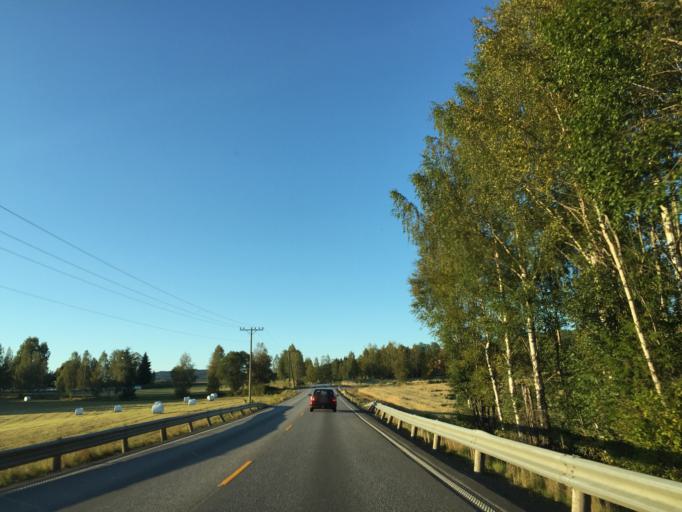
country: NO
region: Hedmark
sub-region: Nord-Odal
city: Sand
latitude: 60.4299
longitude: 11.5128
